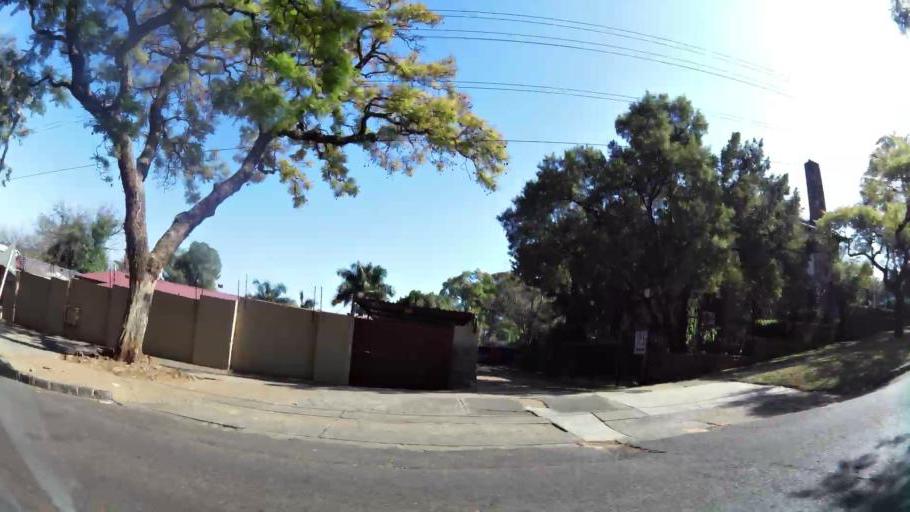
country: ZA
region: Gauteng
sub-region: City of Tshwane Metropolitan Municipality
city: Pretoria
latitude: -25.7426
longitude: 28.2172
